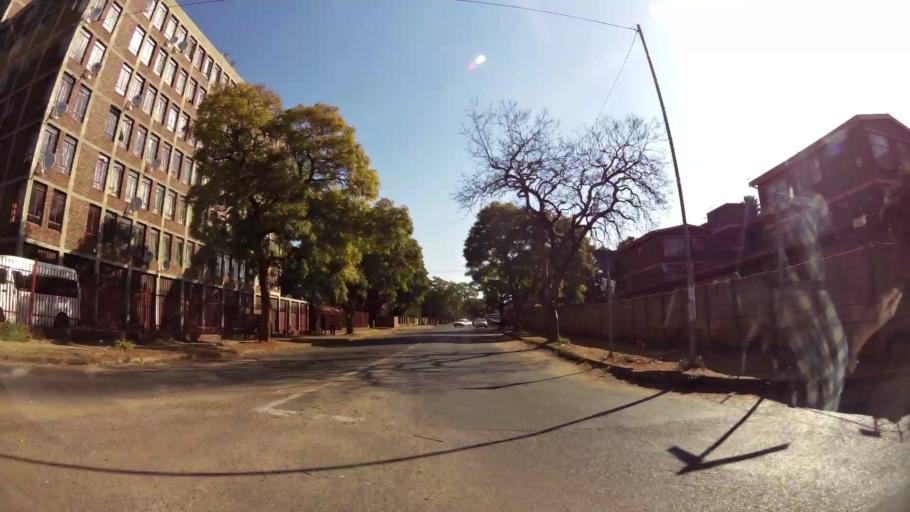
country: ZA
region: Gauteng
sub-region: City of Tshwane Metropolitan Municipality
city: Pretoria
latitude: -25.6801
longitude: 28.1711
